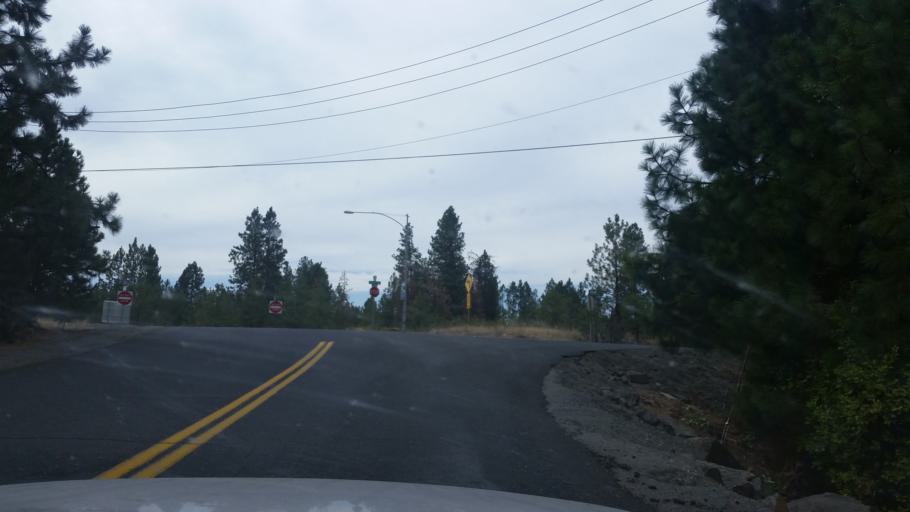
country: US
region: Washington
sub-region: Spokane County
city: Spokane
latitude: 47.6436
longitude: -117.4972
